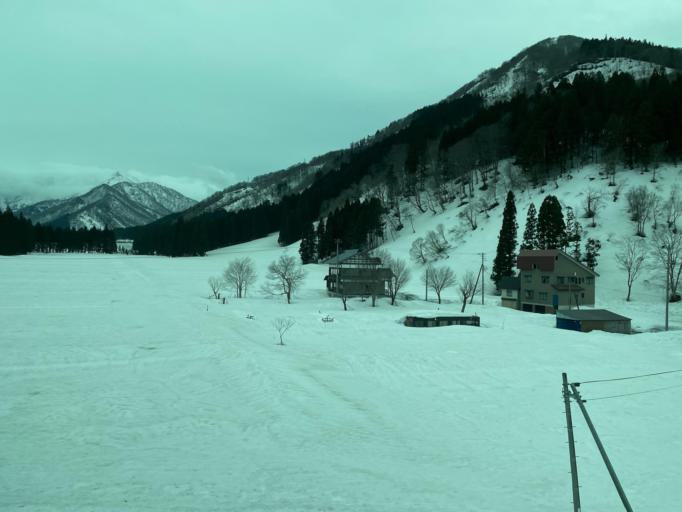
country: JP
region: Niigata
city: Shiozawa
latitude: 36.9021
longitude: 138.8419
